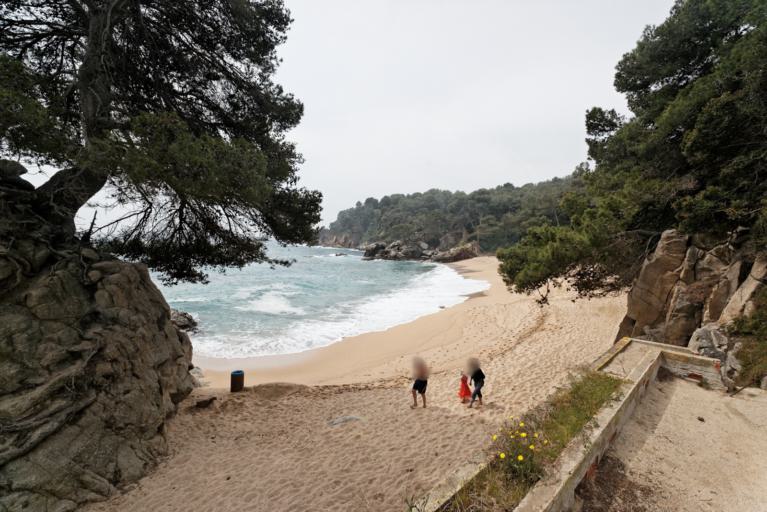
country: ES
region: Catalonia
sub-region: Provincia de Girona
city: Blanes
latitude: 41.6870
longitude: 2.8174
